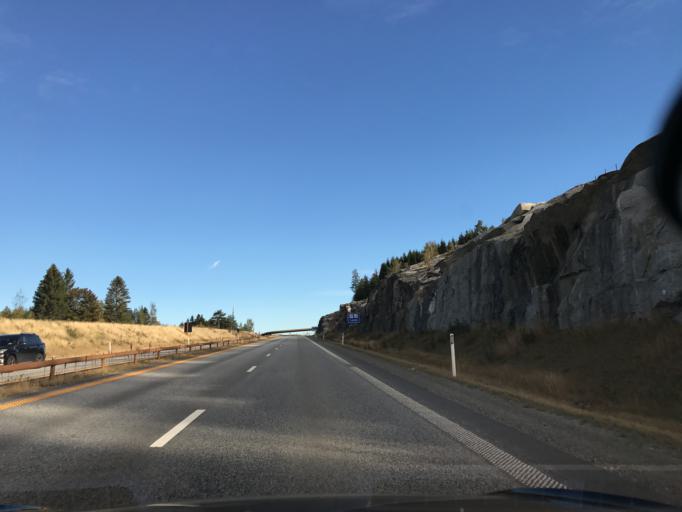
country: NO
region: Hedmark
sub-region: Stange
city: Stange
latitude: 60.5564
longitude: 11.2518
